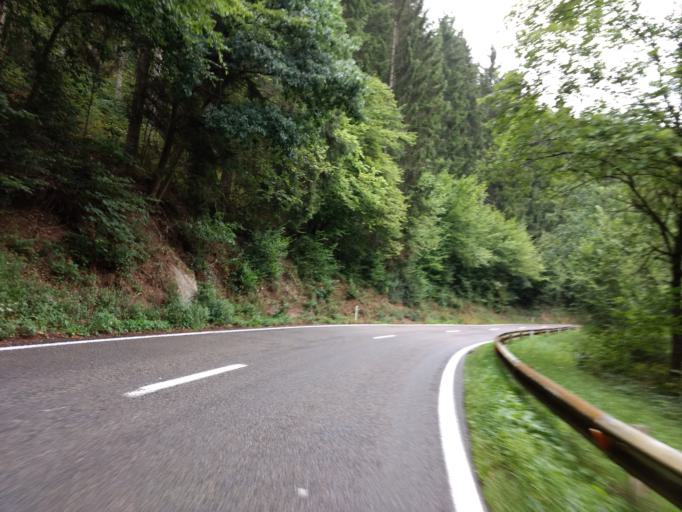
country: BE
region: Wallonia
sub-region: Province du Luxembourg
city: Houffalize
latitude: 50.1345
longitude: 5.7399
